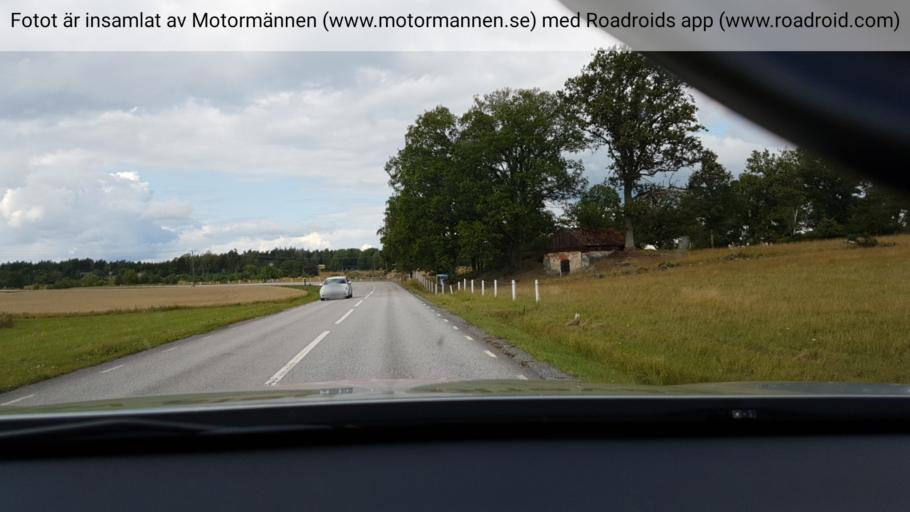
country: SE
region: Stockholm
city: Stenhamra
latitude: 59.3855
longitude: 17.6833
